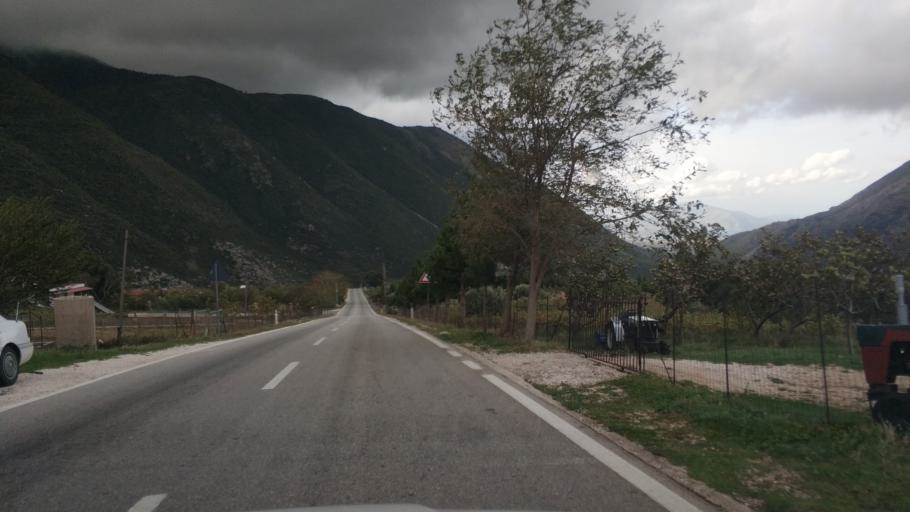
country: AL
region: Vlore
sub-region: Rrethi i Vlores
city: Brataj
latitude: 40.2304
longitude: 19.5710
